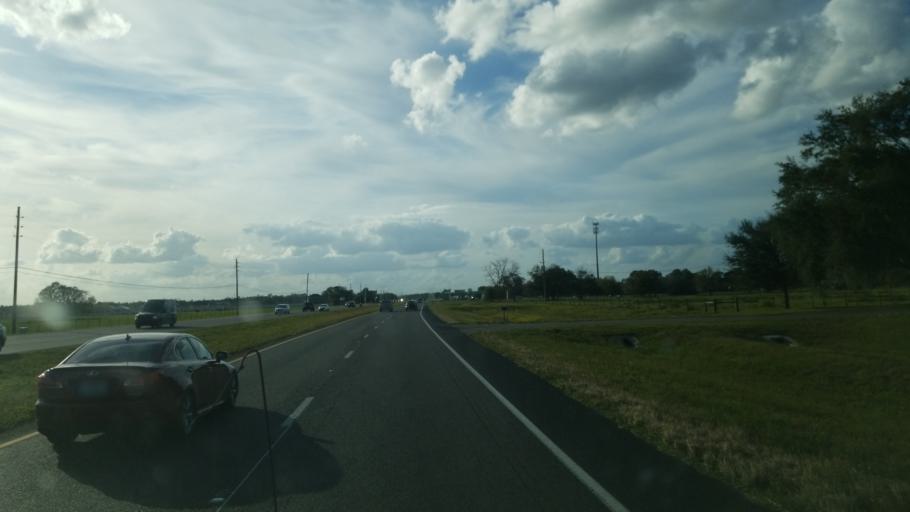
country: US
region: Florida
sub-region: Osceola County
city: Saint Cloud
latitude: 28.2432
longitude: -81.2186
